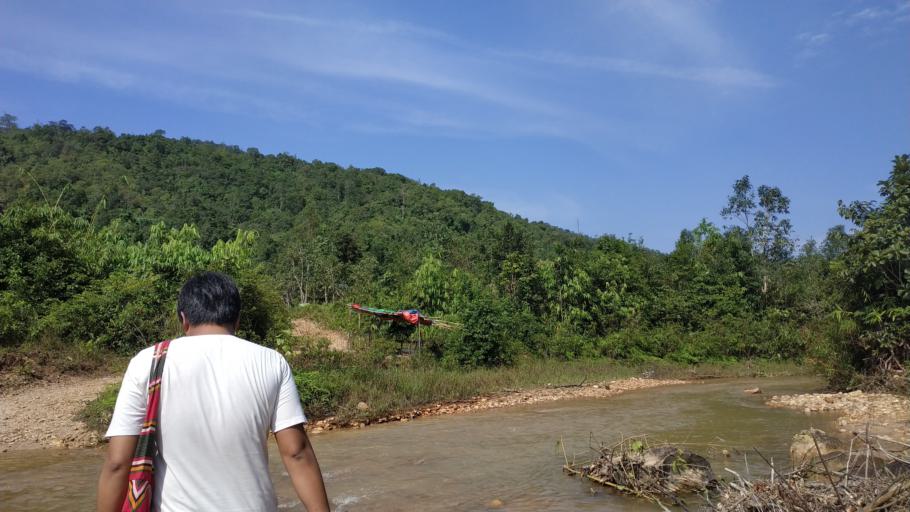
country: MM
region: Tanintharyi
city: Dawei
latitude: 14.5860
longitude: 98.0505
